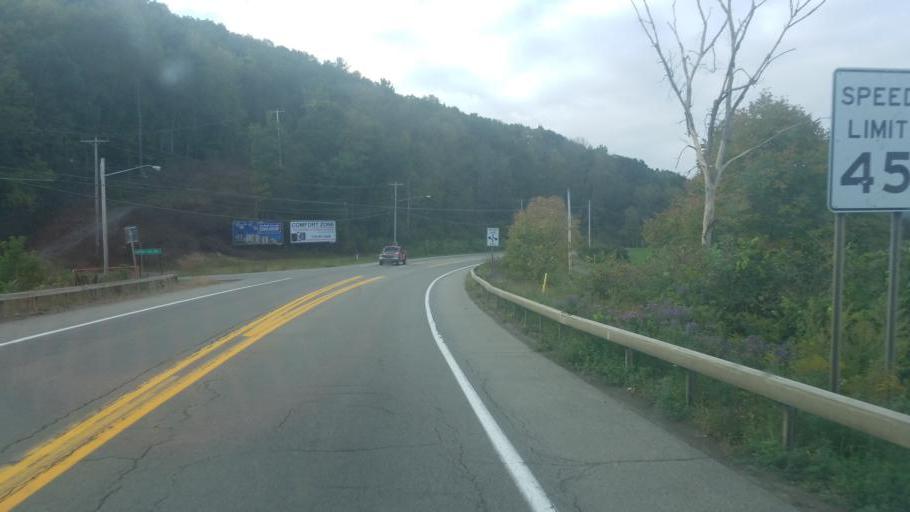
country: US
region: New York
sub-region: Cattaraugus County
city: Olean
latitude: 42.1062
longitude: -78.4179
